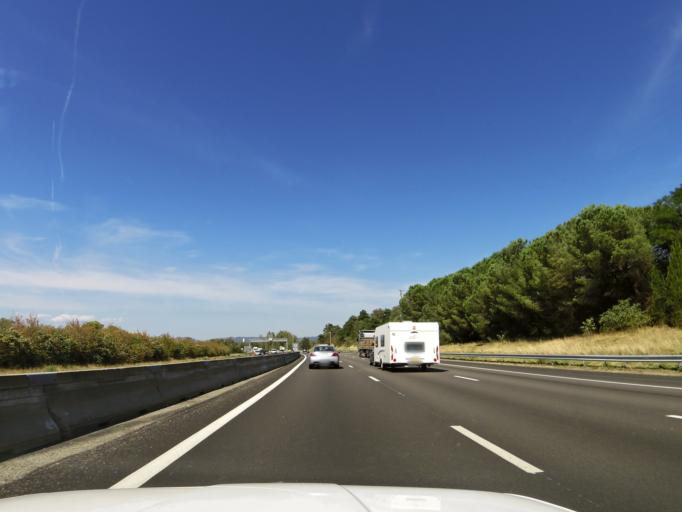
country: FR
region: Rhone-Alpes
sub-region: Departement de l'Ardeche
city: Cornas
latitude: 44.9865
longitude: 4.8822
